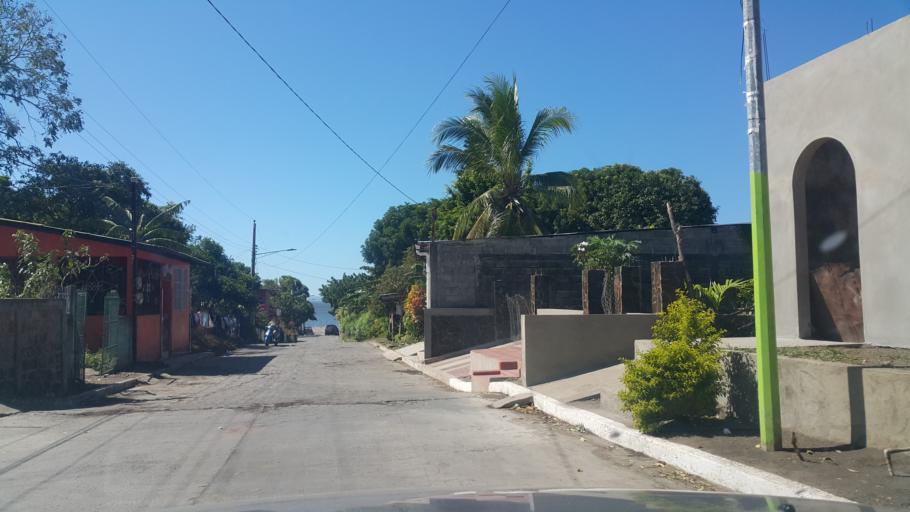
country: NI
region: Rivas
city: Moyogalpa
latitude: 11.5396
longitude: -85.6995
